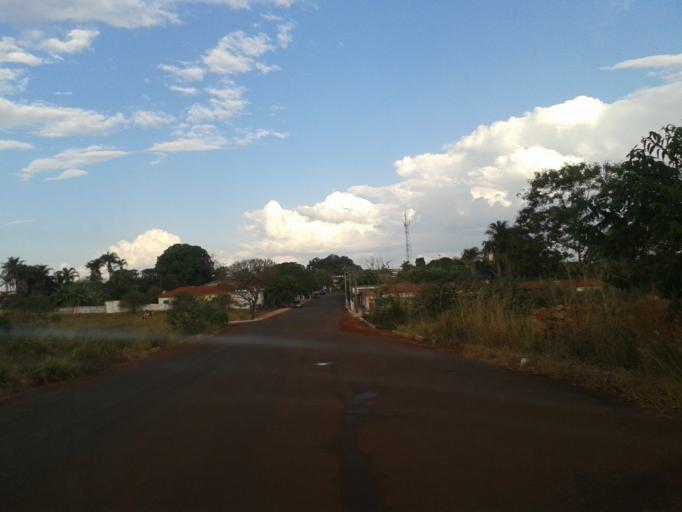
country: BR
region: Minas Gerais
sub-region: Ituiutaba
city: Ituiutaba
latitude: -19.2125
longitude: -49.7899
